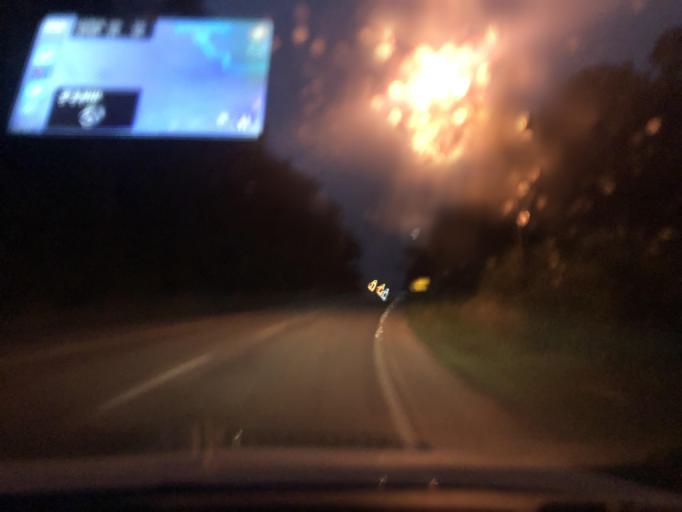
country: BR
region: Santa Catarina
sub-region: Guaramirim
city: Guaramirim
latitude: -26.4970
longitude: -49.0001
